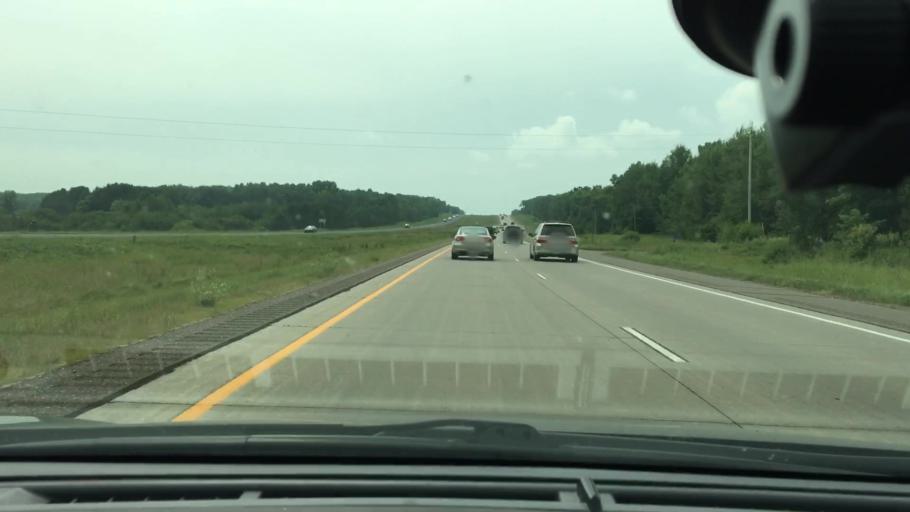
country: US
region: Minnesota
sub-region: Mille Lacs County
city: Vineland
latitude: 46.0007
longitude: -93.6627
